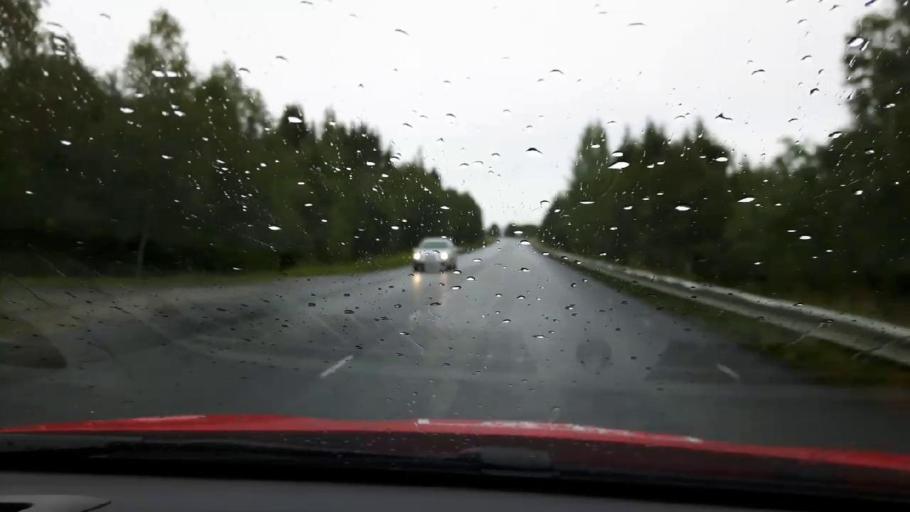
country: SE
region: Jaemtland
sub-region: Are Kommun
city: Are
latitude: 63.3961
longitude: 12.8585
